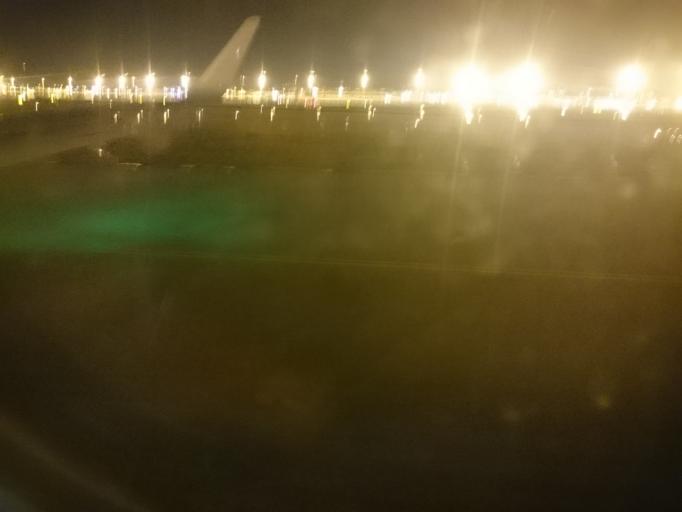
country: ES
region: Catalonia
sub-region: Provincia de Barcelona
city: El Prat de Llobregat
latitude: 41.2957
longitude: 2.0781
